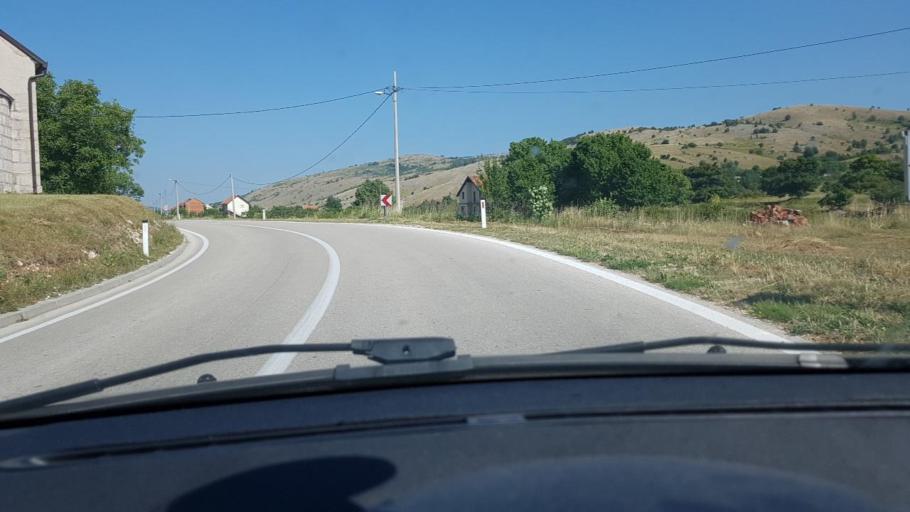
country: BA
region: Federation of Bosnia and Herzegovina
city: Bosansko Grahovo
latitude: 44.1188
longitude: 16.5365
